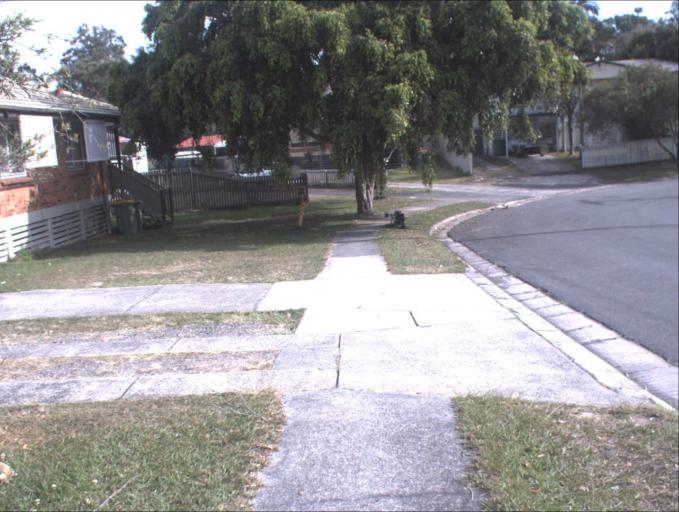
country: AU
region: Queensland
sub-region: Logan
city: Woodridge
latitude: -27.6332
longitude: 153.0999
